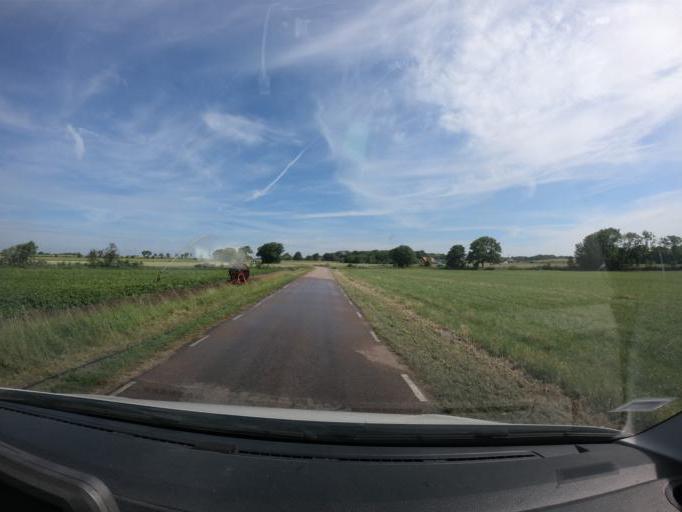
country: SE
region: Skane
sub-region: Angelholms Kommun
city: Vejbystrand
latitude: 56.4030
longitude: 12.6578
